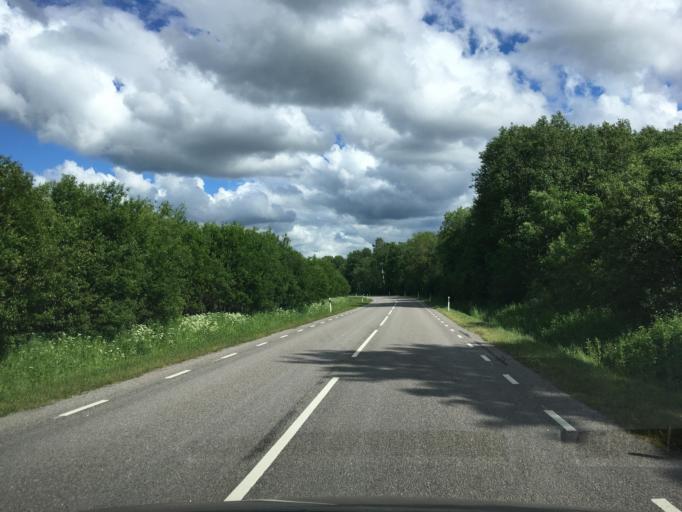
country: EE
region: Paernumaa
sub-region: Halinga vald
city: Parnu-Jaagupi
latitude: 58.6719
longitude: 24.6273
